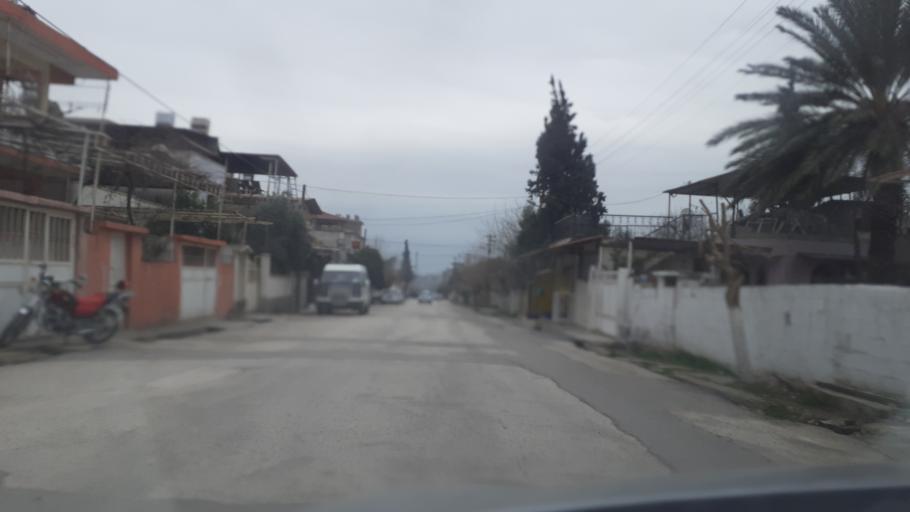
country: TR
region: Hatay
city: Kirikhan
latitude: 36.4894
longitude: 36.3558
